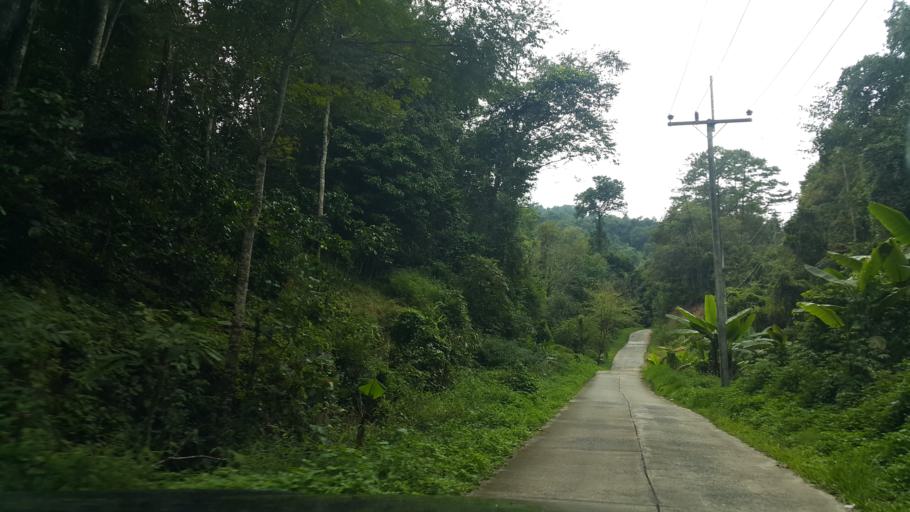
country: TH
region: Lampang
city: Wang Nuea
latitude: 19.0823
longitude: 99.3829
